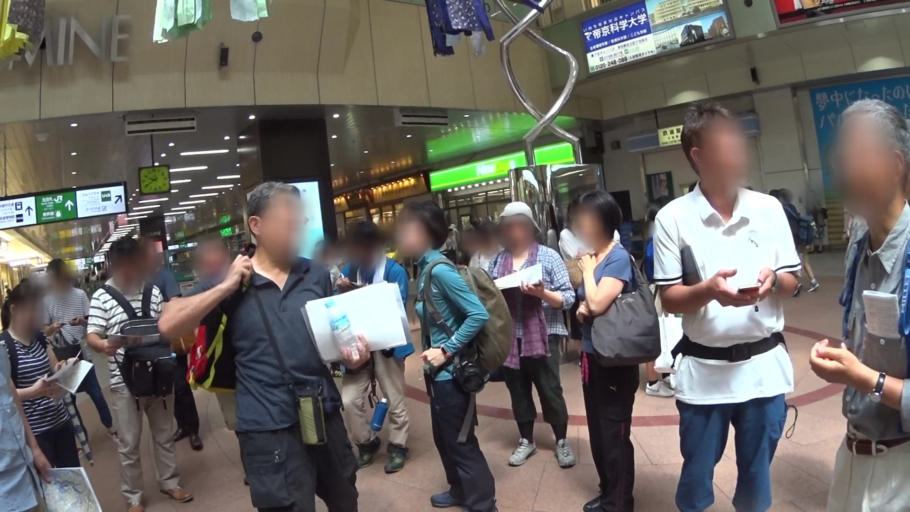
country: JP
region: Saitama
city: Yono
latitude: 35.9056
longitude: 139.6229
